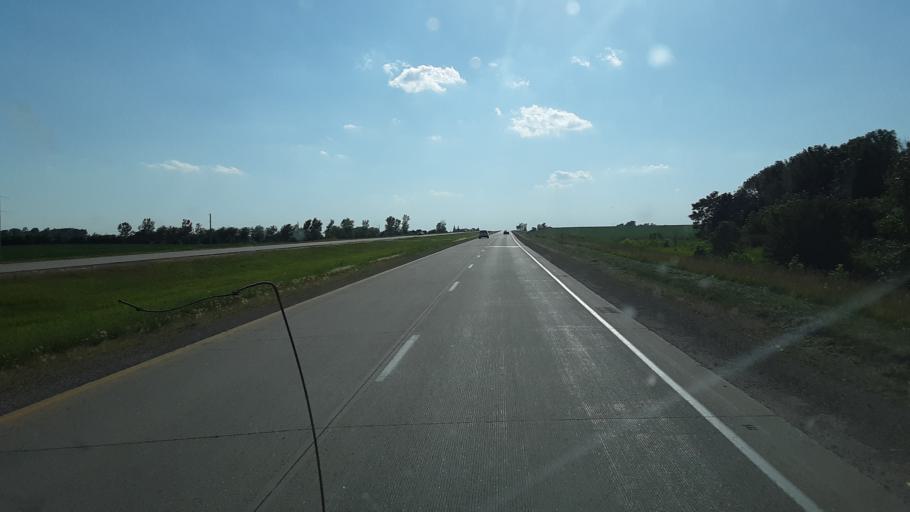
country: US
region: Iowa
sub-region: Grundy County
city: Dike
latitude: 42.4632
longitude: -92.7295
